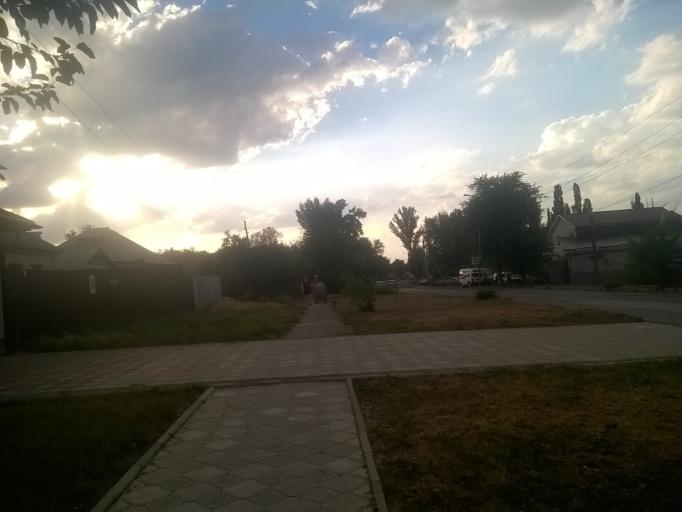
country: RU
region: Rostov
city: Donetsk
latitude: 48.3365
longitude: 39.9561
